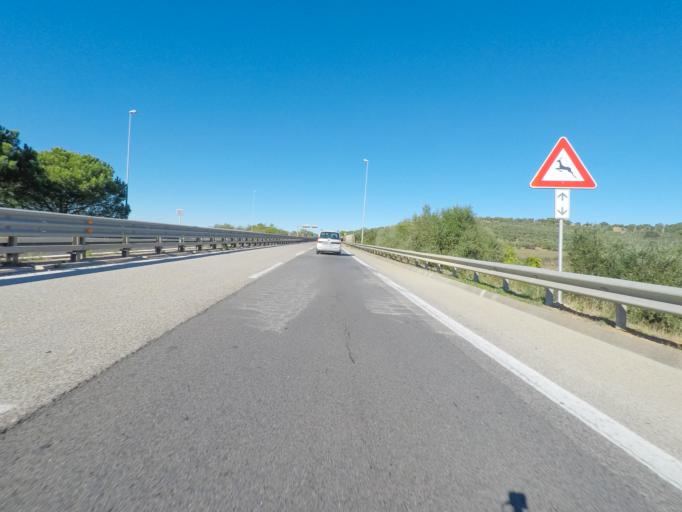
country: IT
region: Tuscany
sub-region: Provincia di Grosseto
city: Grosseto
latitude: 42.7327
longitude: 11.1362
